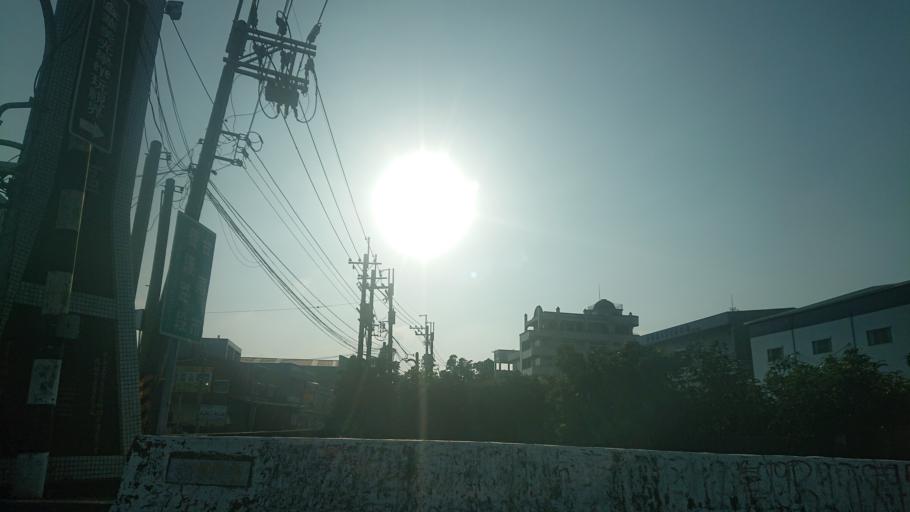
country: TW
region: Taiwan
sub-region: Tainan
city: Tainan
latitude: 23.0740
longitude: 120.2138
